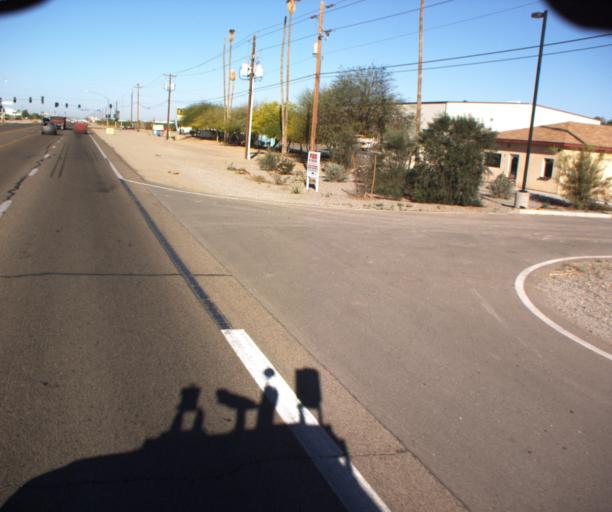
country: US
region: Arizona
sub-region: Yuma County
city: Yuma
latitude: 32.6699
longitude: -114.5622
